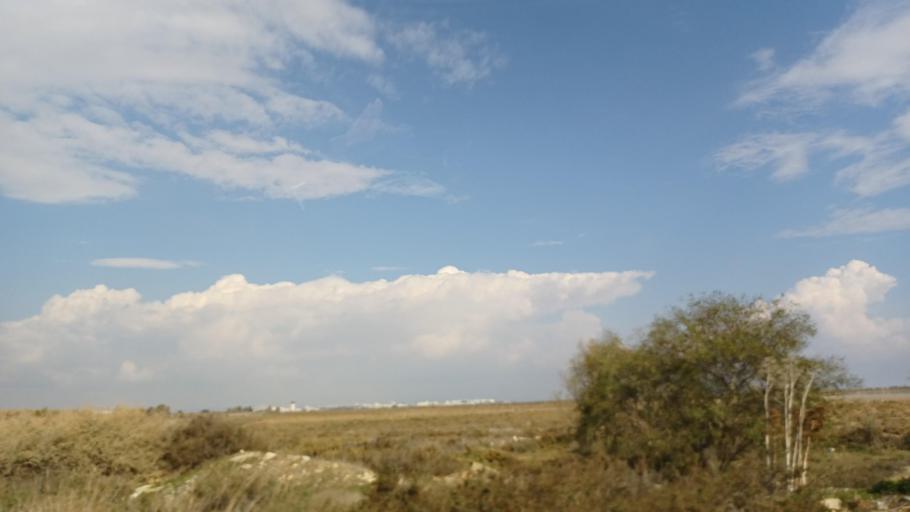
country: CY
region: Larnaka
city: Meneou
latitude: 34.8506
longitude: 33.6108
